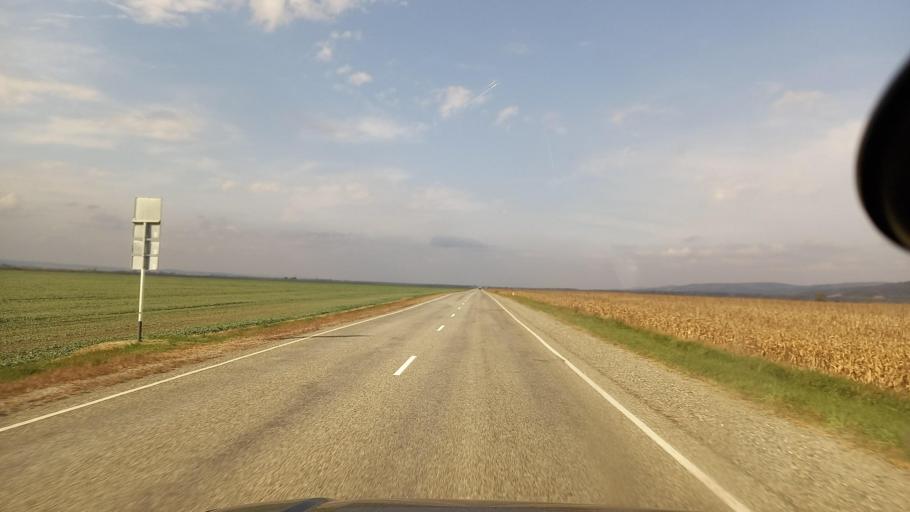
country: RU
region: Krasnodarskiy
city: Perepravnaya
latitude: 44.3030
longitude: 40.8605
